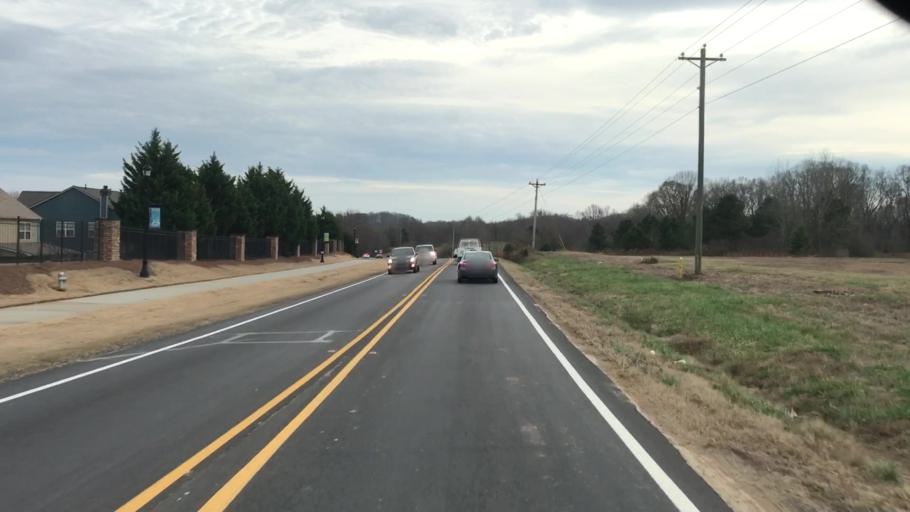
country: US
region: Georgia
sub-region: Jackson County
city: Braselton
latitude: 34.1183
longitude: -83.8251
